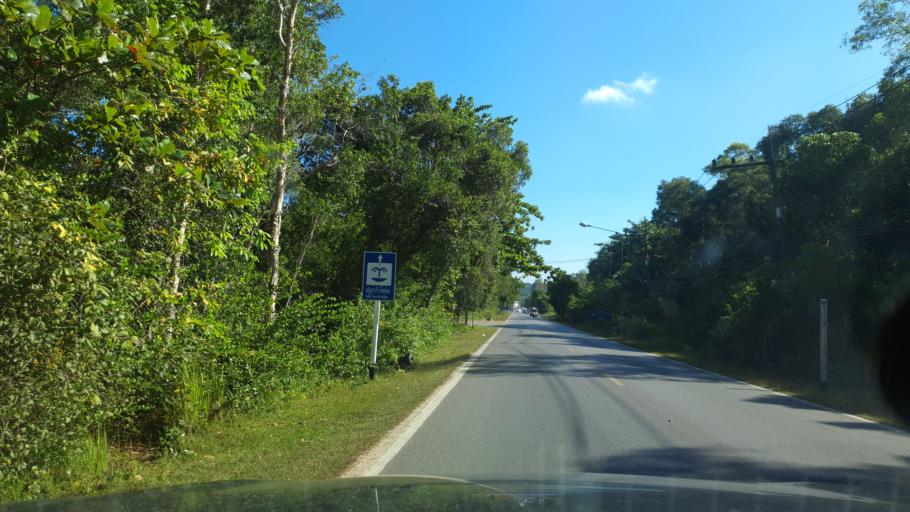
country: TH
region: Phangnga
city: Ban Ao Nang
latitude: 8.0488
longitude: 98.8035
